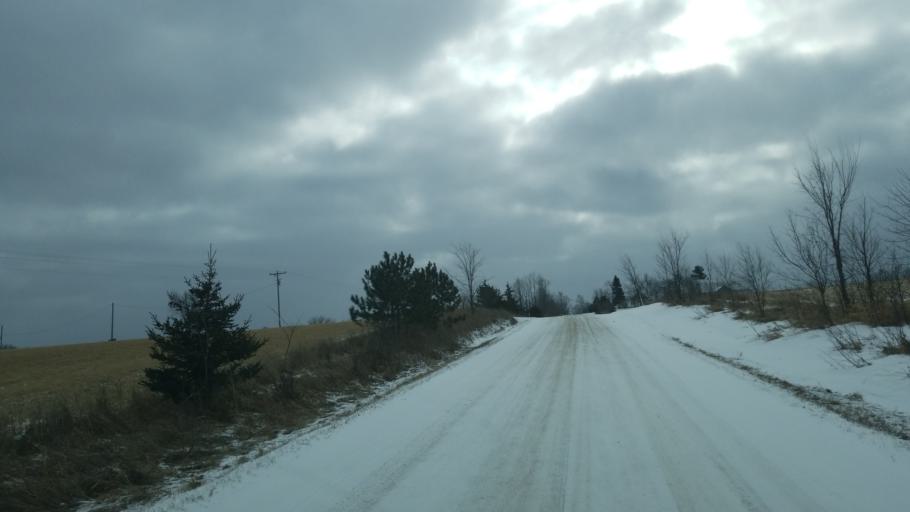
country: US
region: Michigan
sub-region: Osceola County
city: Evart
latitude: 44.0285
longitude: -85.2269
